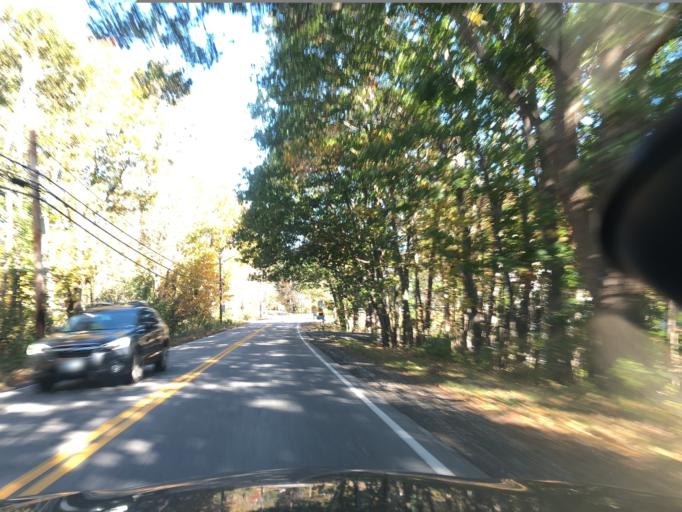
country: US
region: New Hampshire
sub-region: Rockingham County
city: Exeter
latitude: 43.0289
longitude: -70.9444
